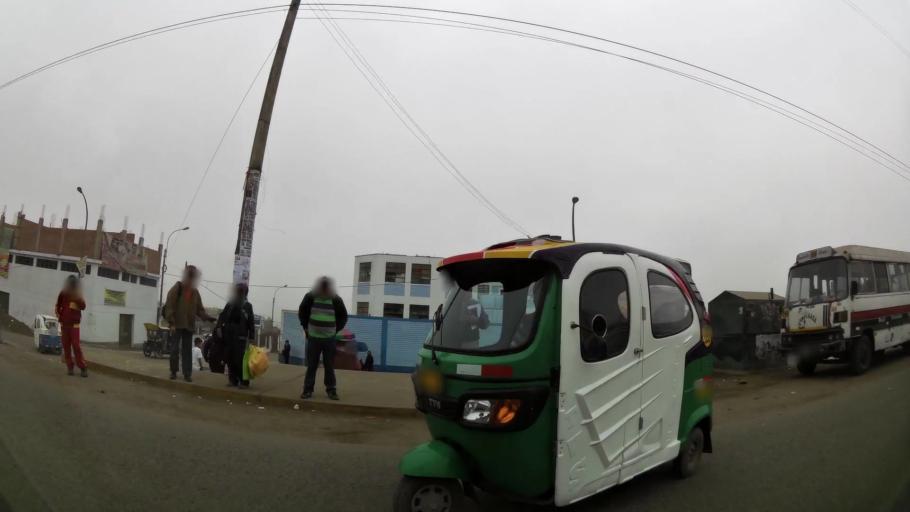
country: PE
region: Lima
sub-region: Lima
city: Urb. Santo Domingo
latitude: -11.8745
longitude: -77.0161
